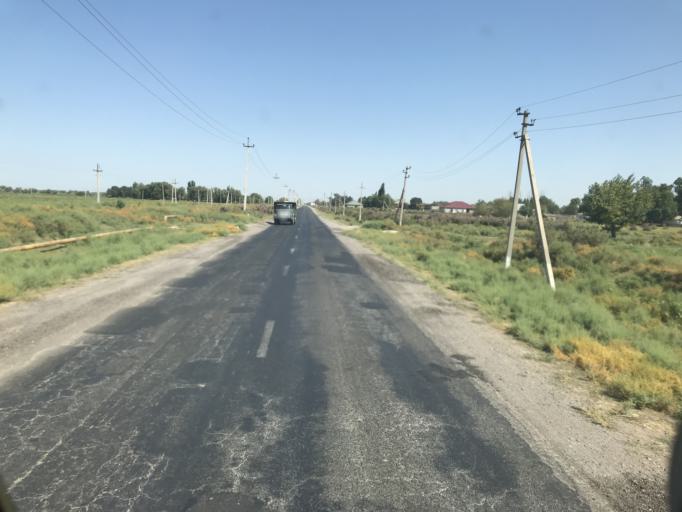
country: KZ
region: Ongtustik Qazaqstan
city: Ilyich
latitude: 40.8886
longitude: 68.4881
